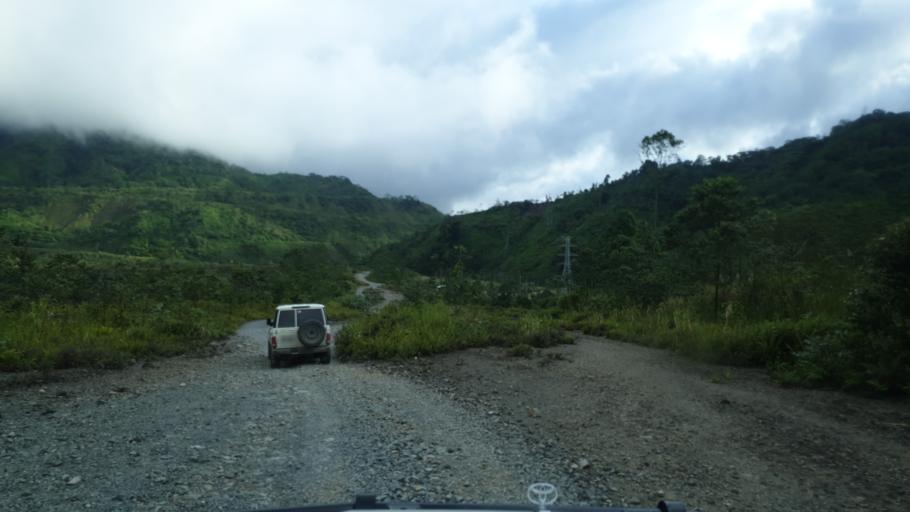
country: PG
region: Bougainville
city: Panguna
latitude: -6.3090
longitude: 155.4884
